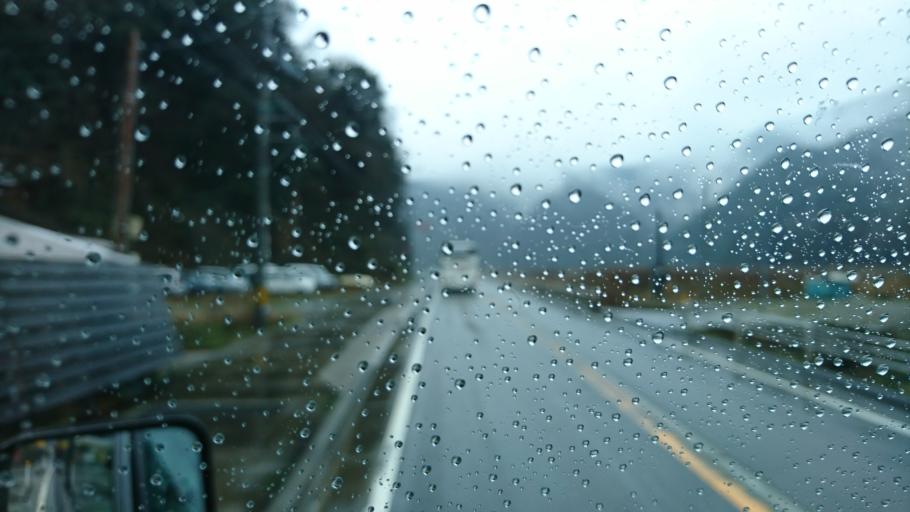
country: JP
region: Tottori
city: Tottori
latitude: 35.5858
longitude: 134.4898
